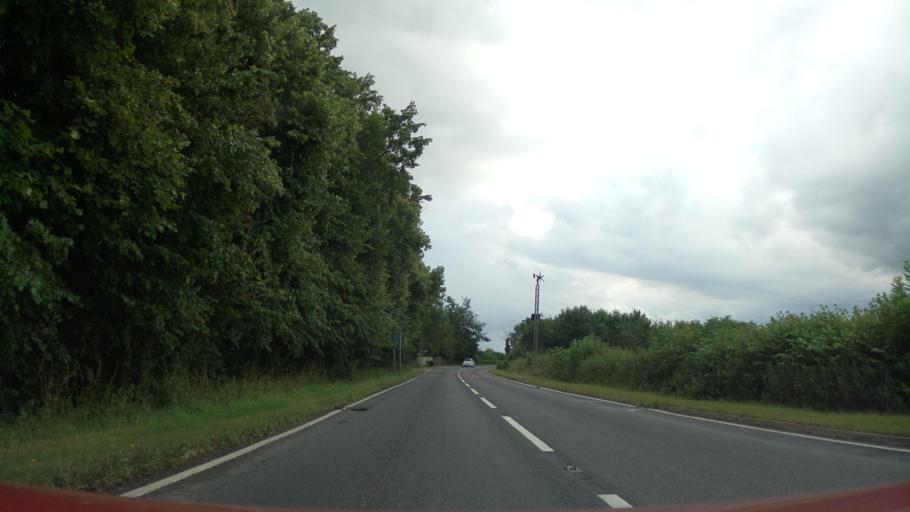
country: GB
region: England
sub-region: Warwickshire
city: Long Itchington
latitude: 52.2737
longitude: -1.3659
